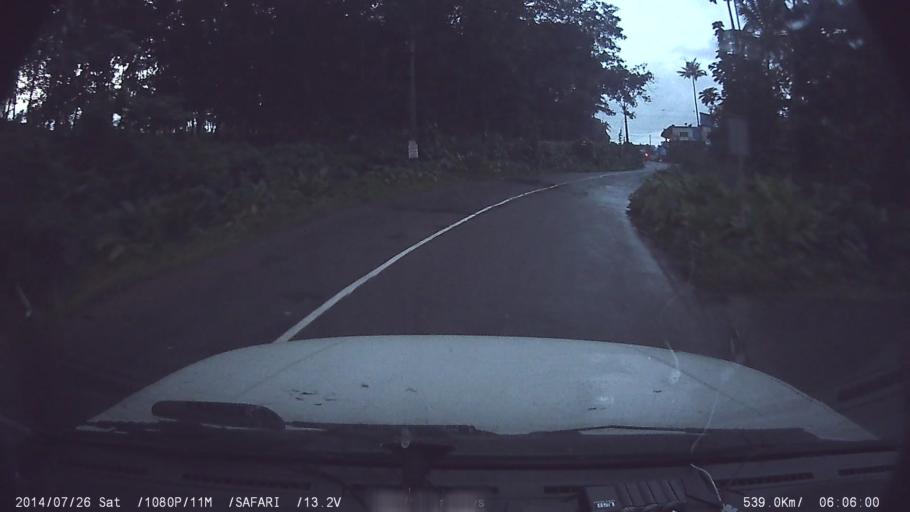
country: IN
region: Kerala
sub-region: Ernakulam
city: Muvattupuzha
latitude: 9.8903
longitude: 76.5895
